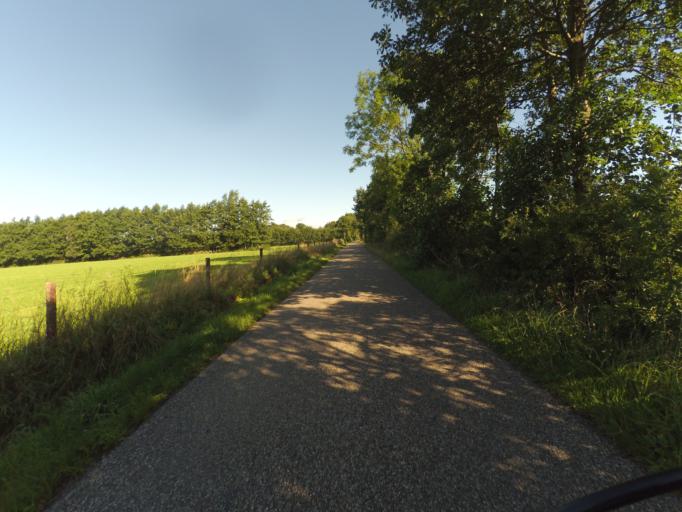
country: NL
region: Friesland
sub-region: Gemeente Achtkarspelen
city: Buitenpost
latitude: 53.2640
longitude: 6.1443
